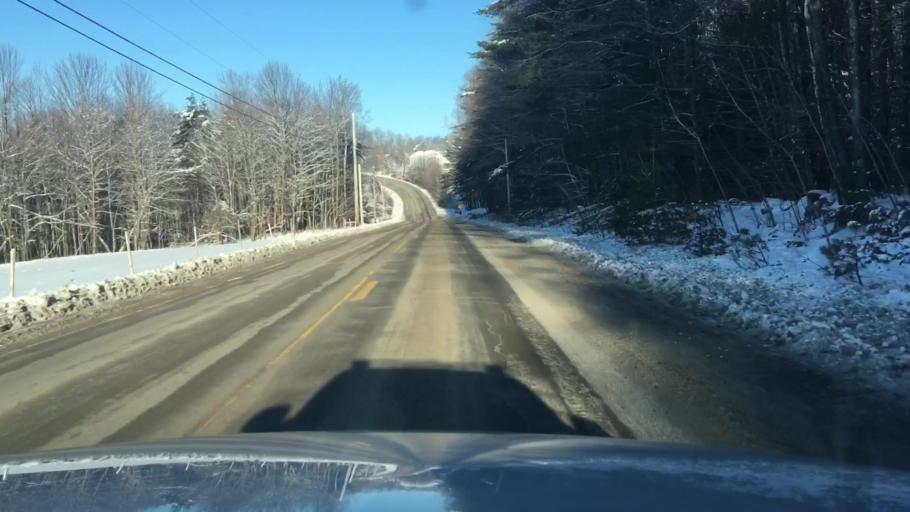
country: US
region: Maine
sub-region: Kennebec County
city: Readfield
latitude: 44.4273
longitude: -69.9351
